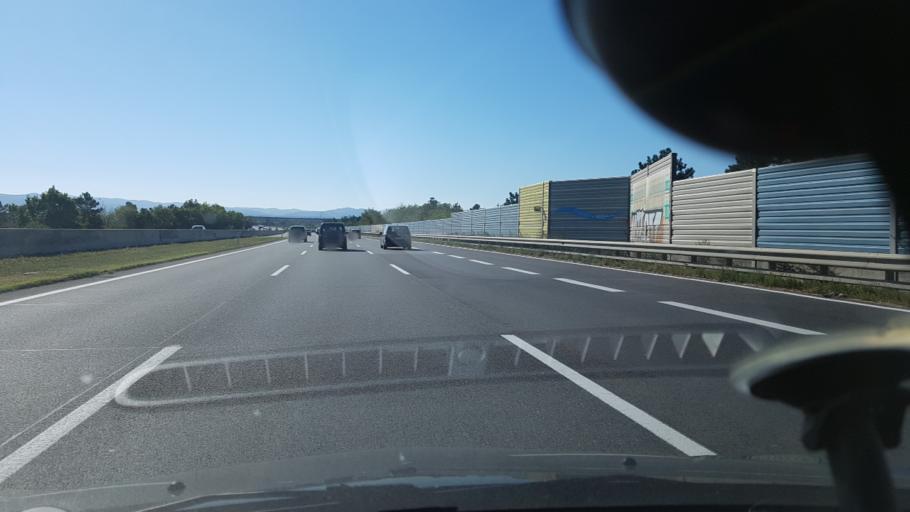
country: AT
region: Lower Austria
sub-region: Politischer Bezirk Wiener Neustadt
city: Weikersdorf am Steinfelde
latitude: 47.8314
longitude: 16.1830
